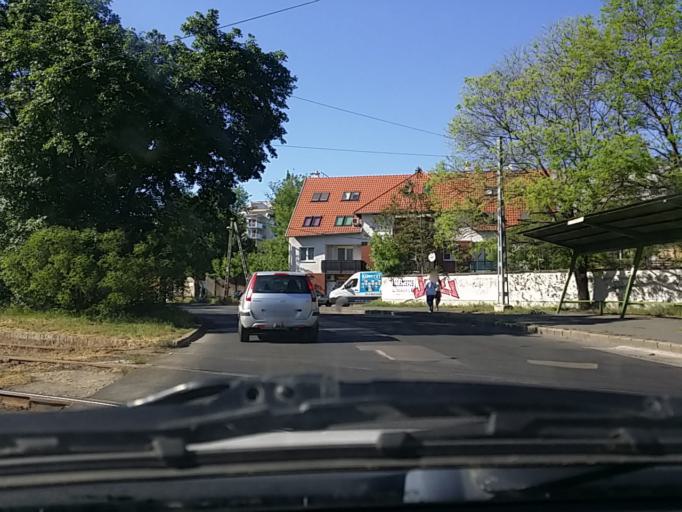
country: HU
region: Budapest
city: Budapest IV. keruelet
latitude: 47.5532
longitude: 19.0925
